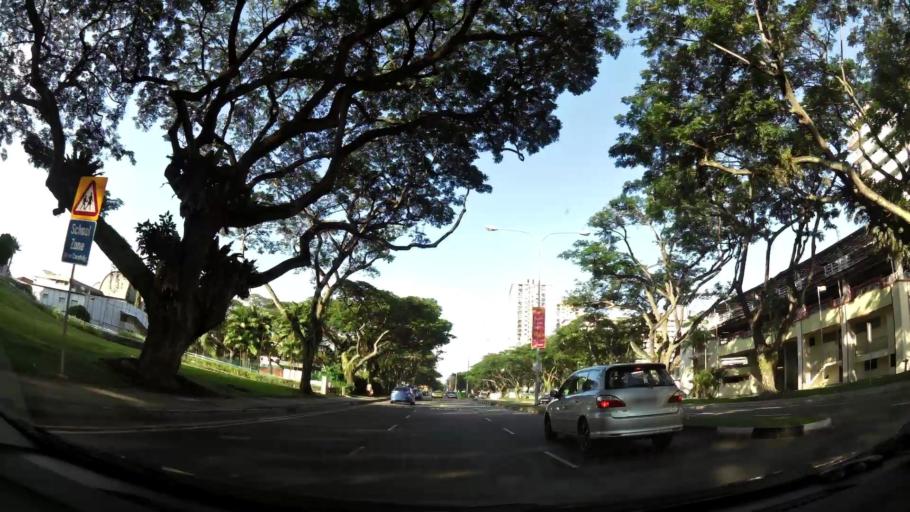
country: SG
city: Singapore
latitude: 1.3200
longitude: 103.9367
